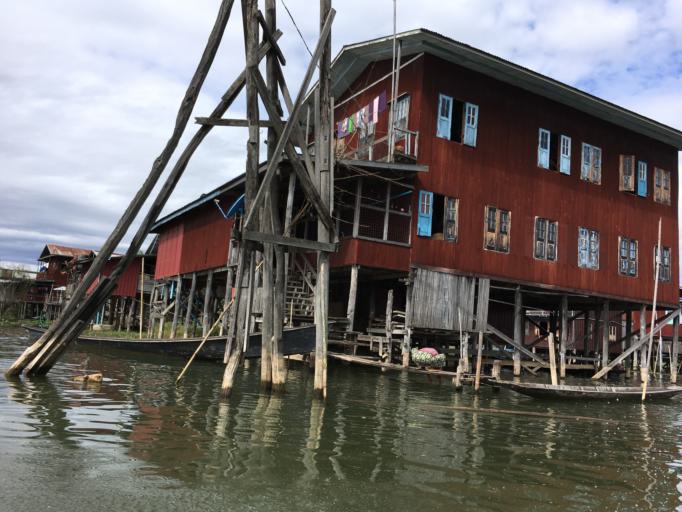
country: MM
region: Shan
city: Taunggyi
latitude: 20.4505
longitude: 96.9052
